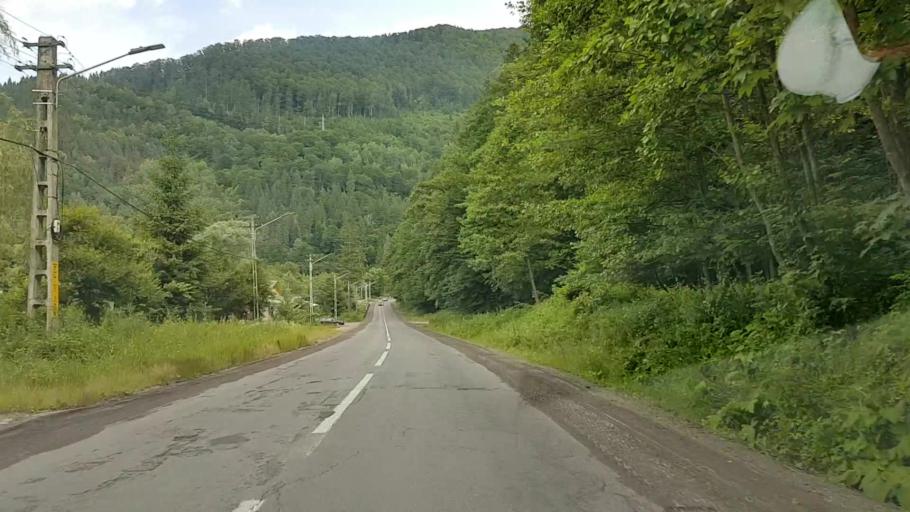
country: RO
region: Neamt
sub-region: Comuna Bicaz
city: Dodeni
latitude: 46.9359
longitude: 26.0941
